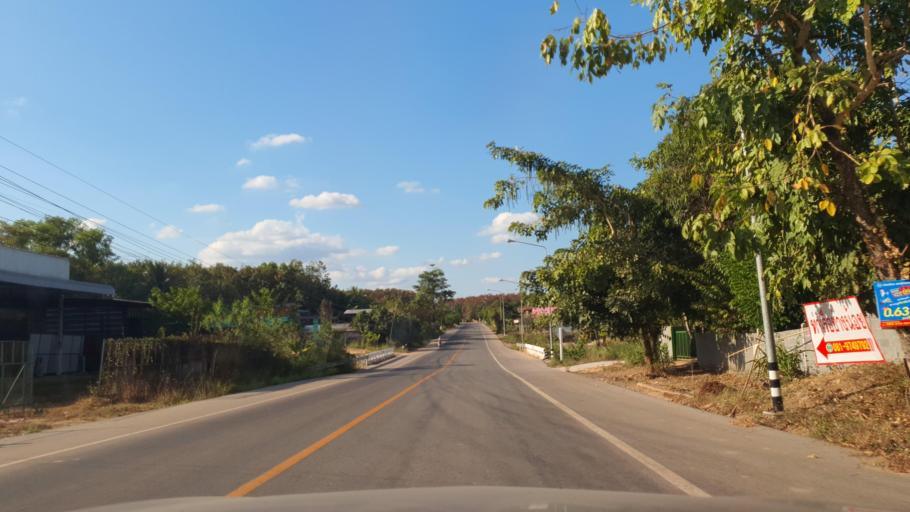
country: TH
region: Nong Khai
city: Bueng Khong Long
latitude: 18.0083
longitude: 104.0092
